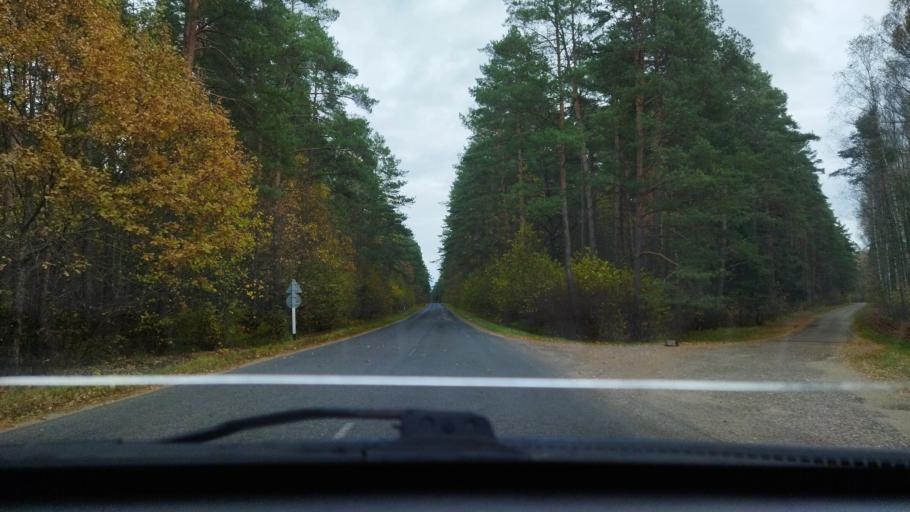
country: BY
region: Minsk
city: Svir
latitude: 54.8166
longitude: 26.1805
